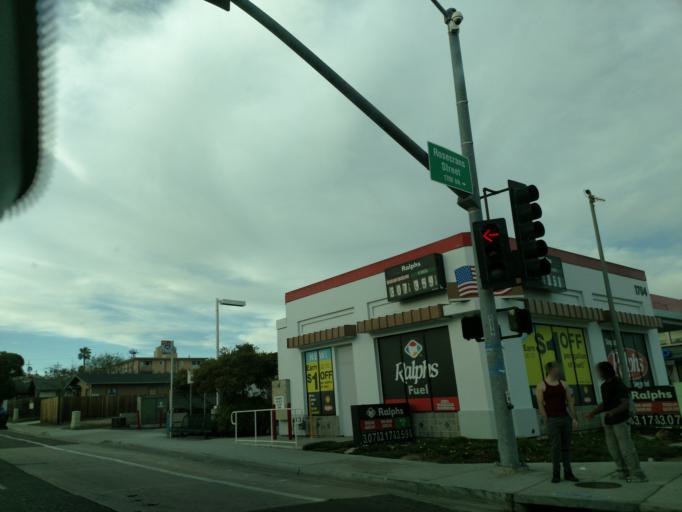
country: US
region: California
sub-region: San Diego County
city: Coronado
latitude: 32.7287
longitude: -117.2259
